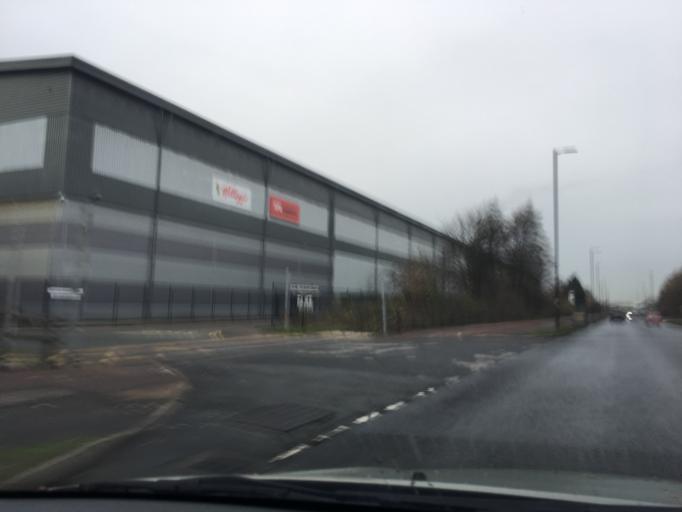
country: GB
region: England
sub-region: Trafford
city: Stretford
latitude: 53.4583
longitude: -2.3230
